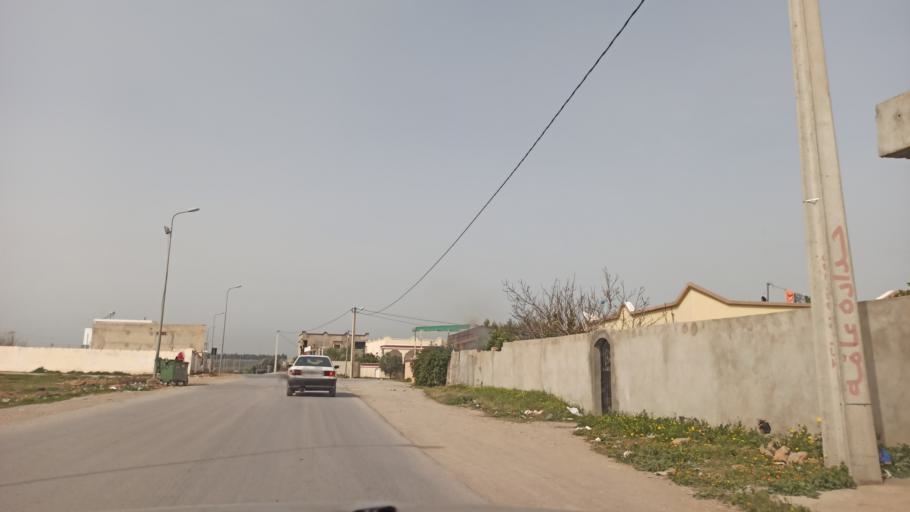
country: TN
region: Zaghwan
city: Zaghouan
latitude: 36.4174
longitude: 10.1208
